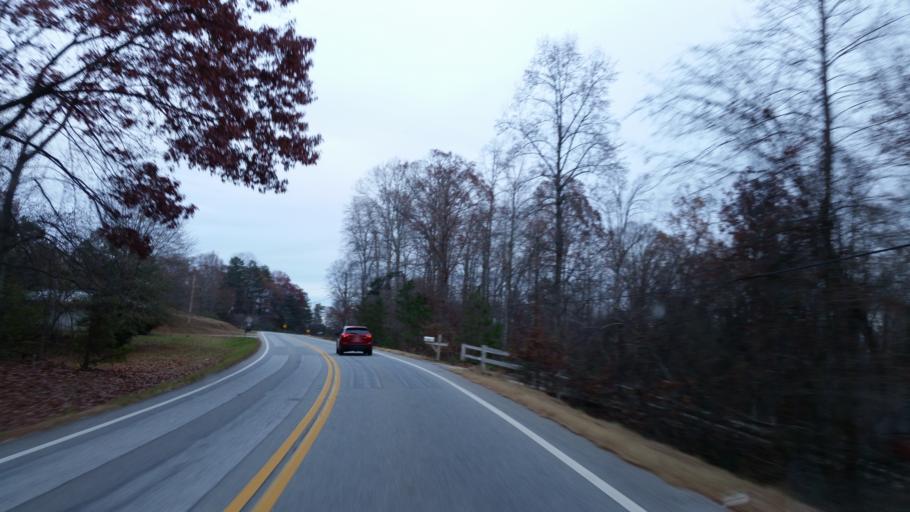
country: US
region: Georgia
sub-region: Dawson County
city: Dawsonville
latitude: 34.4242
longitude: -84.0490
